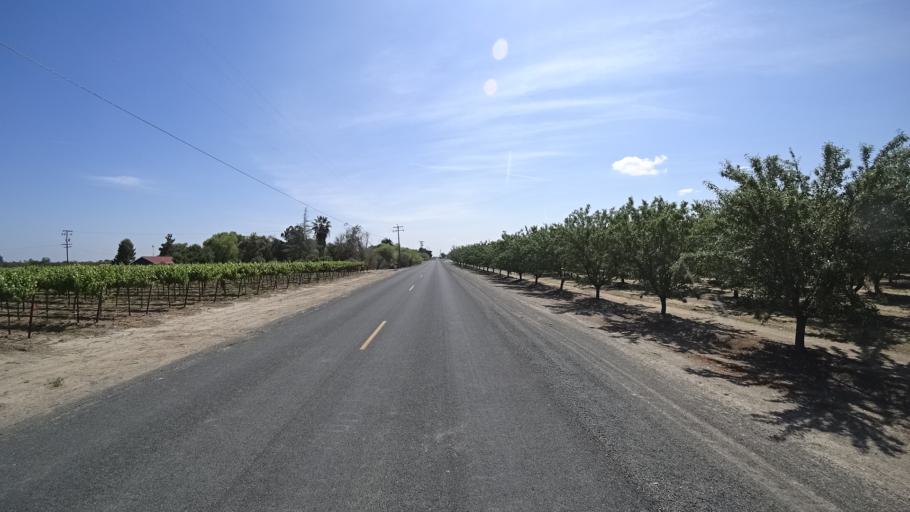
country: US
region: California
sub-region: Kings County
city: Armona
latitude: 36.2692
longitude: -119.7234
